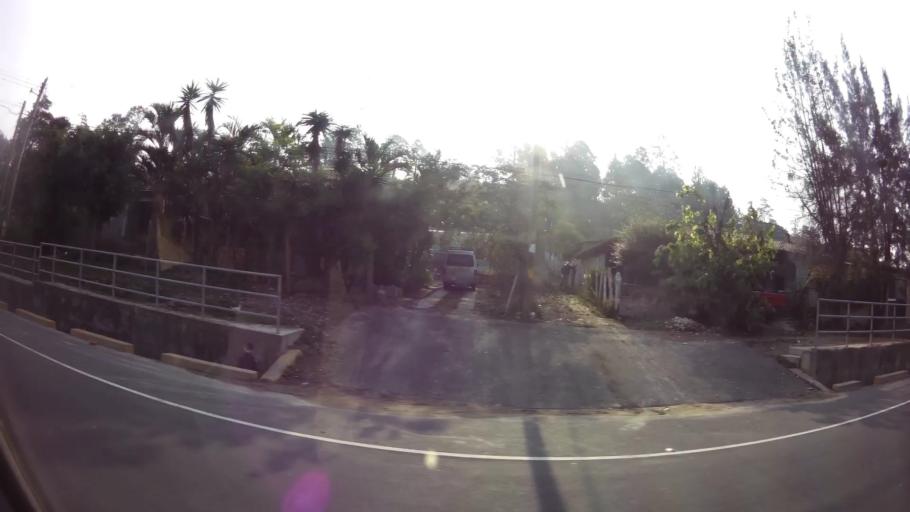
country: HN
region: Francisco Morazan
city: Zambrano
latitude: 14.2745
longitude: -87.4052
